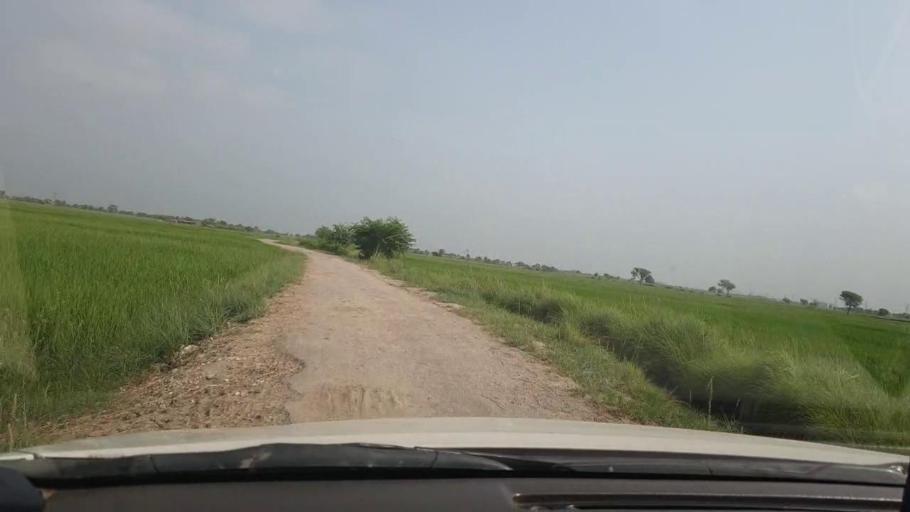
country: PK
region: Sindh
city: Shikarpur
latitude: 27.9848
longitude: 68.6093
